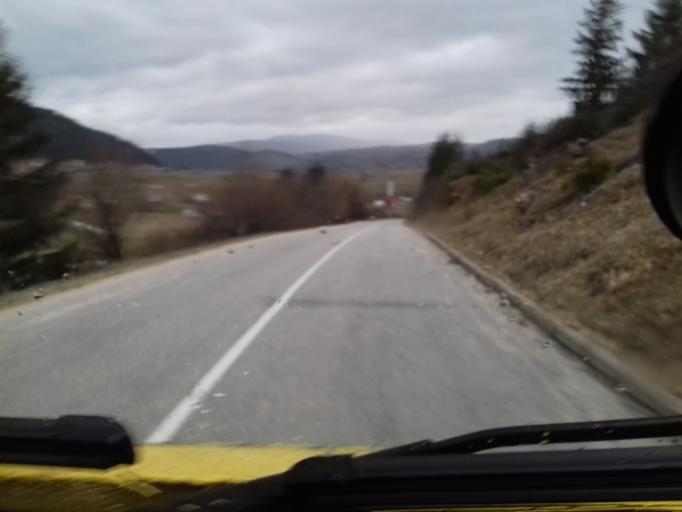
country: BA
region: Federation of Bosnia and Herzegovina
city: Turbe
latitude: 44.3122
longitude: 17.5328
